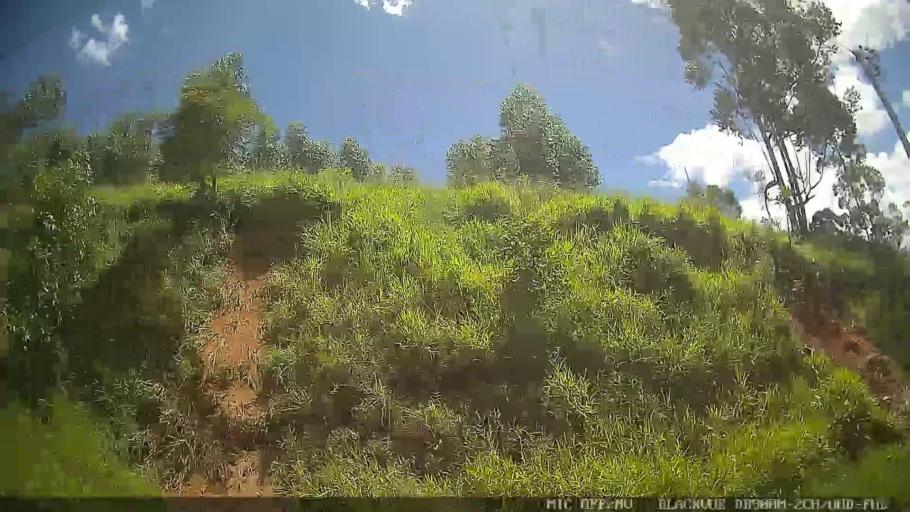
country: BR
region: Sao Paulo
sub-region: Santa Branca
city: Santa Branca
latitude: -23.5248
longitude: -45.7592
